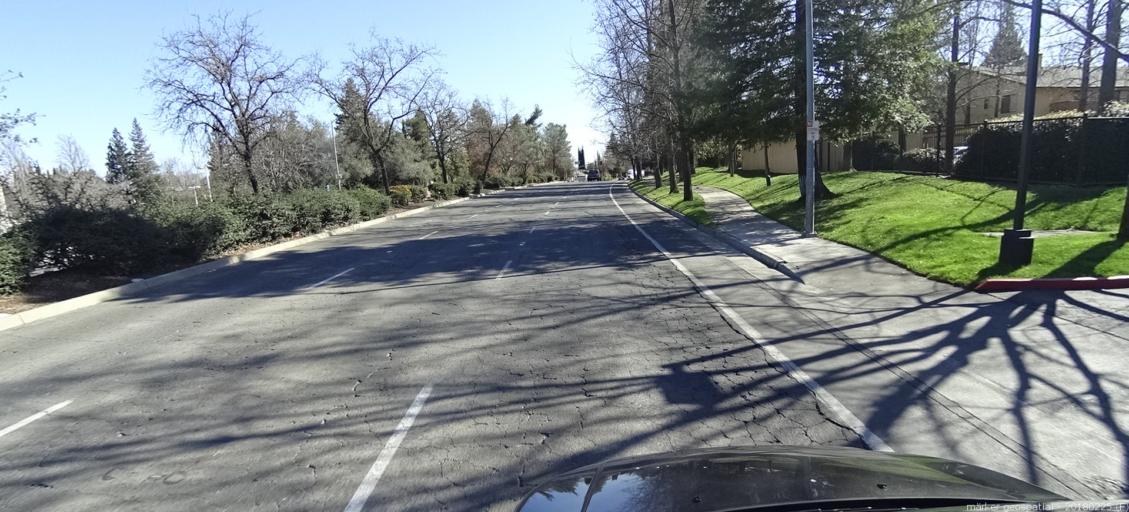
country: US
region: California
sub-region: Sacramento County
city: North Highlands
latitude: 38.7184
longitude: -121.3801
